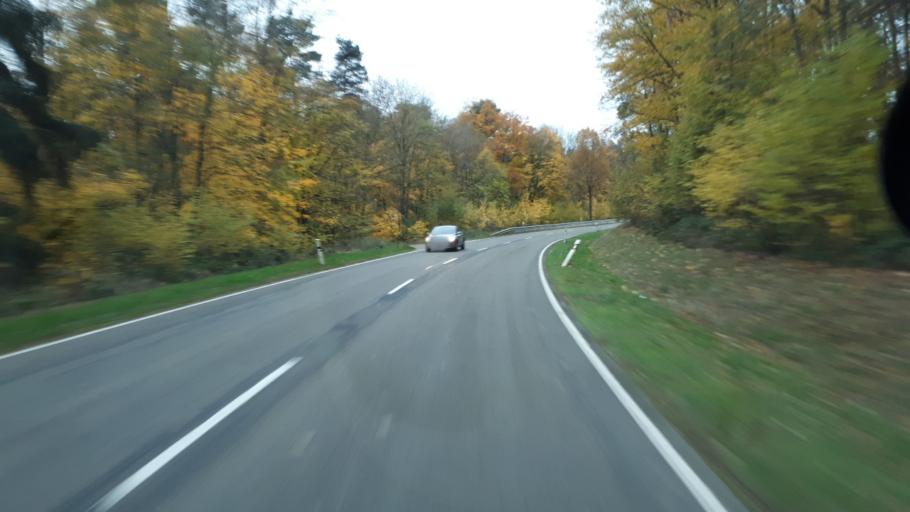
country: DE
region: Rheinland-Pfalz
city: Kaisersesch
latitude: 50.2158
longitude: 7.1434
